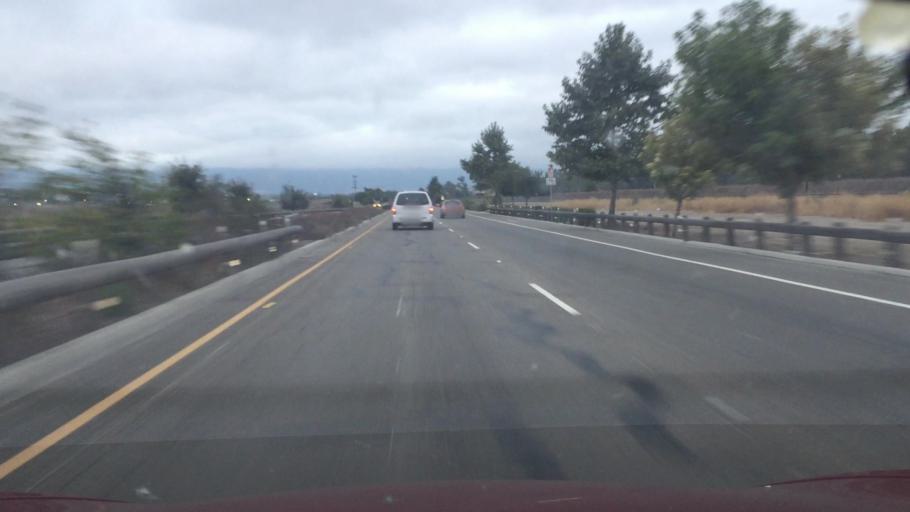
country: US
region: California
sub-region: Alameda County
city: Livermore
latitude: 37.6758
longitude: -121.8087
